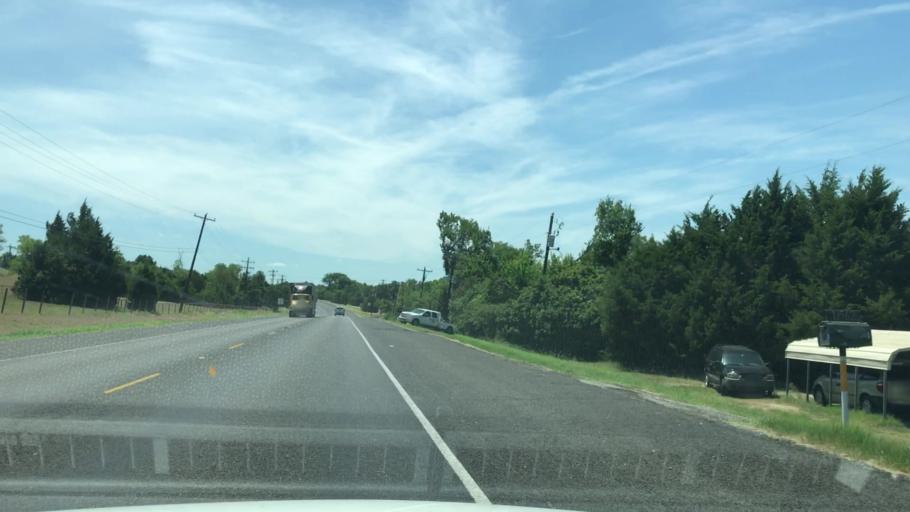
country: US
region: Texas
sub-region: Collin County
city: Lavon
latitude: 33.0004
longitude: -96.4641
